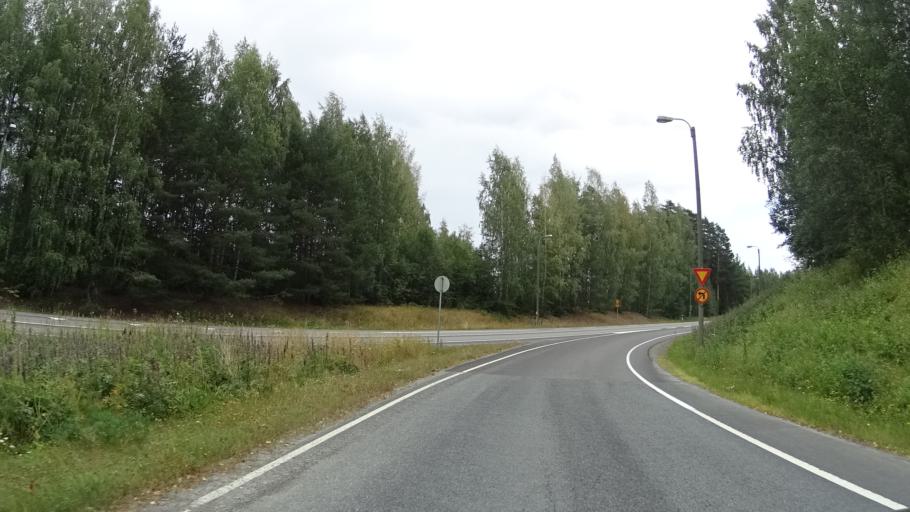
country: FI
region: Pirkanmaa
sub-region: Tampere
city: Kangasala
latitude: 61.4475
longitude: 24.1038
